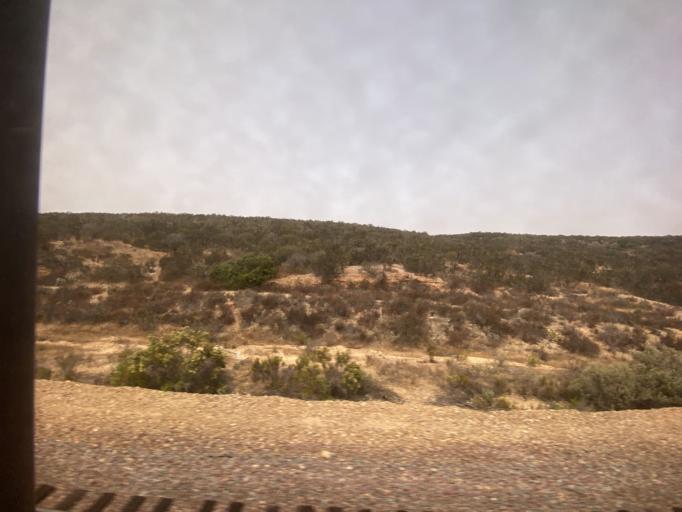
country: US
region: California
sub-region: San Diego County
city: La Jolla
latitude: 32.8711
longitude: -117.1787
